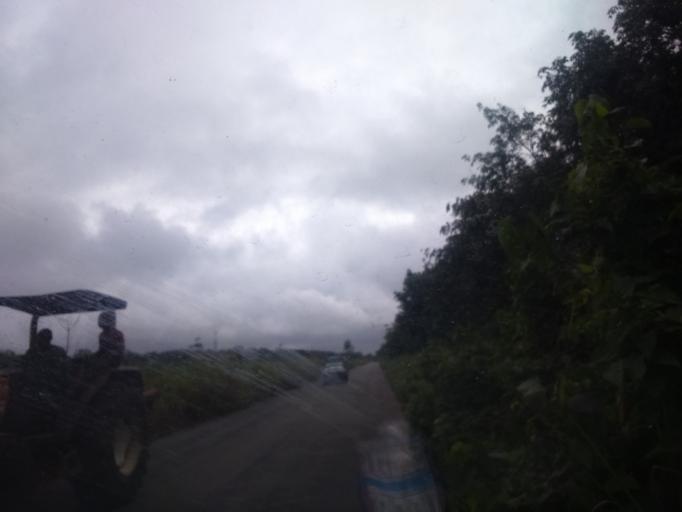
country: CI
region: Sud-Comoe
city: Bonoua
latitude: 5.2807
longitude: -3.4851
